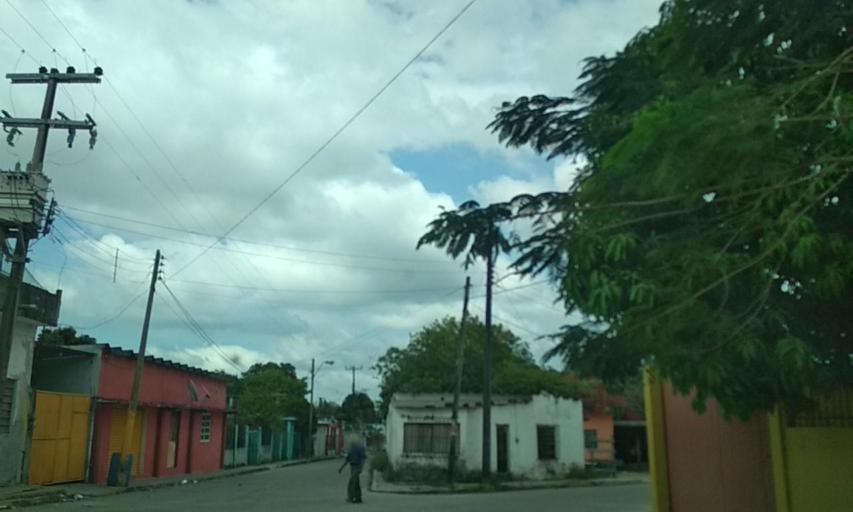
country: MX
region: Veracruz
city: Las Choapas
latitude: 17.8958
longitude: -94.1048
